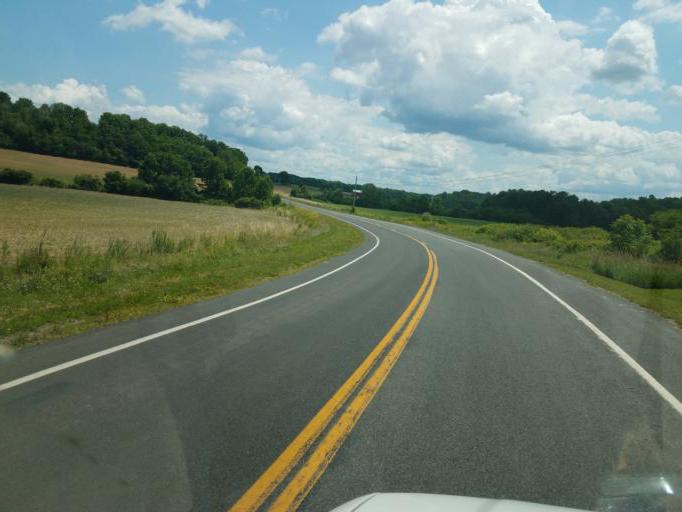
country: US
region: New York
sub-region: Wayne County
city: Clyde
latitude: 43.0610
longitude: -76.8558
